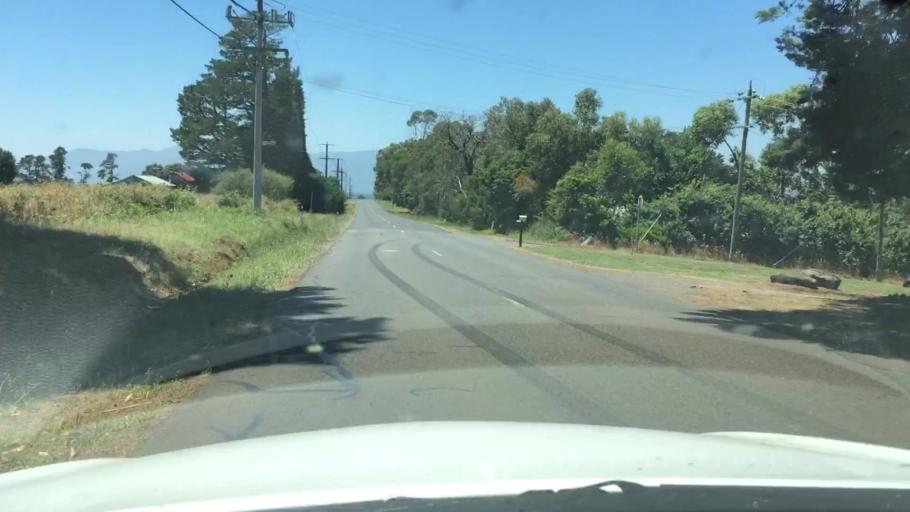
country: AU
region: Victoria
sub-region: Yarra Ranges
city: Mount Evelyn
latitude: -37.8108
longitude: 145.4276
